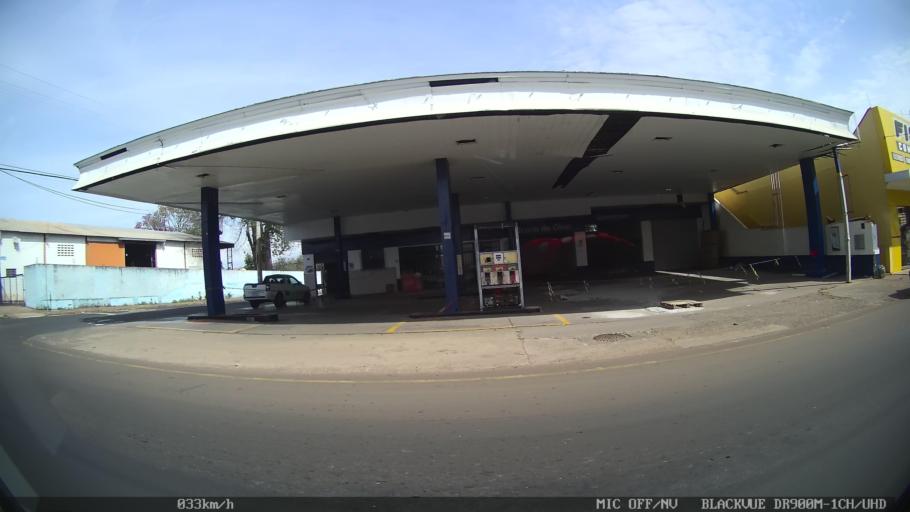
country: BR
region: Sao Paulo
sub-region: Piracicaba
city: Piracicaba
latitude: -22.7447
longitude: -47.6510
